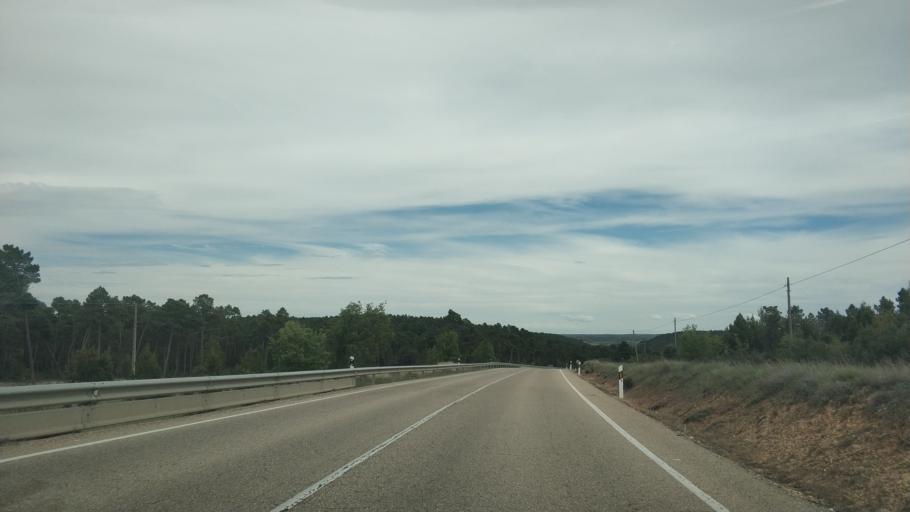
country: ES
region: Castille and Leon
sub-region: Provincia de Soria
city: Bayubas de Abajo
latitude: 41.5198
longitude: -2.9316
